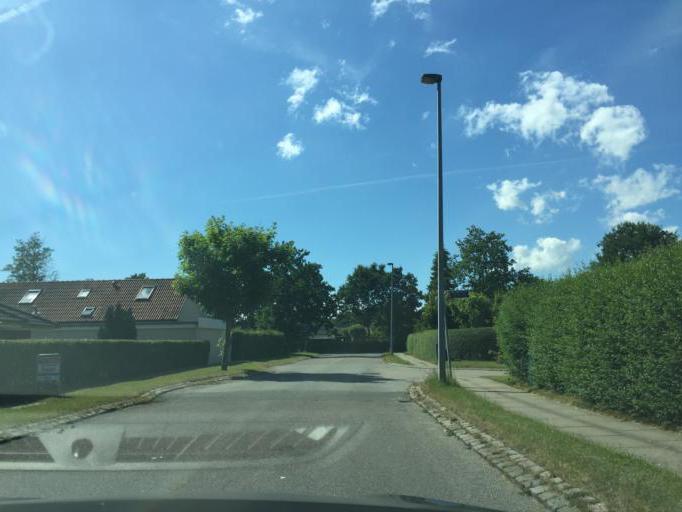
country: DK
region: South Denmark
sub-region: Odense Kommune
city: Neder Holluf
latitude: 55.3735
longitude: 10.4691
